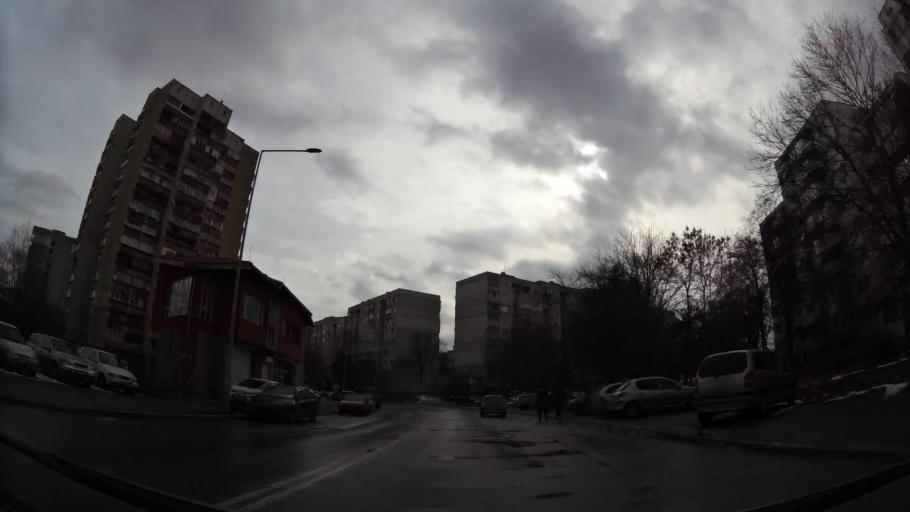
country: BG
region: Sofiya
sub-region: Obshtina Bozhurishte
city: Bozhurishte
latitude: 42.7160
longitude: 23.2426
